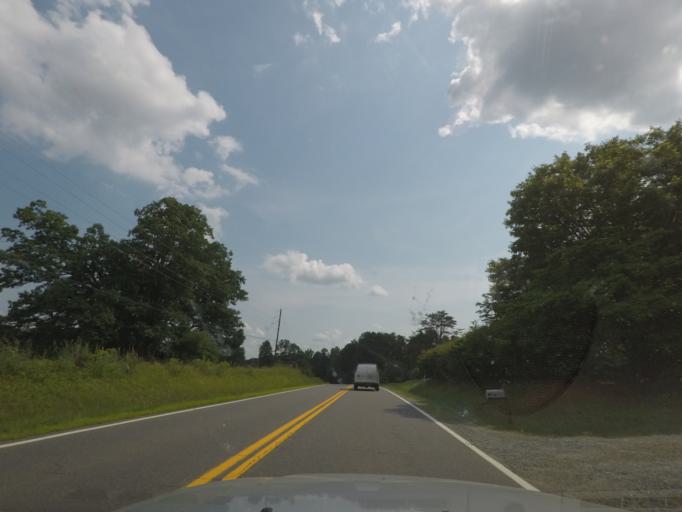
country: US
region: Virginia
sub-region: Fluvanna County
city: Palmyra
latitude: 37.9085
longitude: -78.2570
